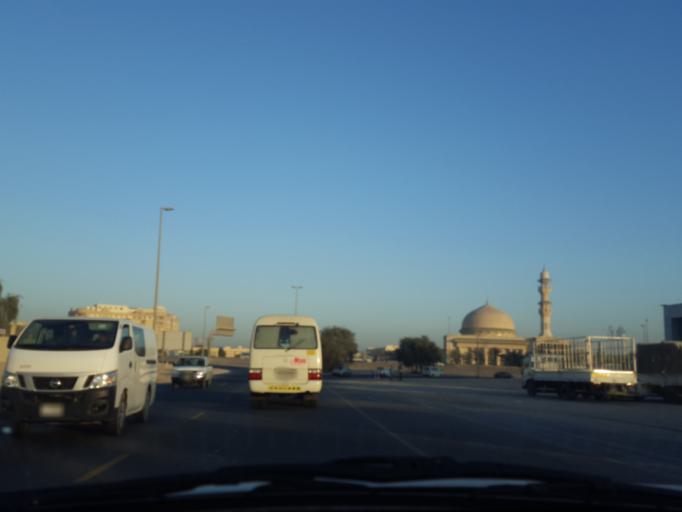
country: AE
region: Dubai
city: Dubai
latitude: 25.1423
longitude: 55.2560
